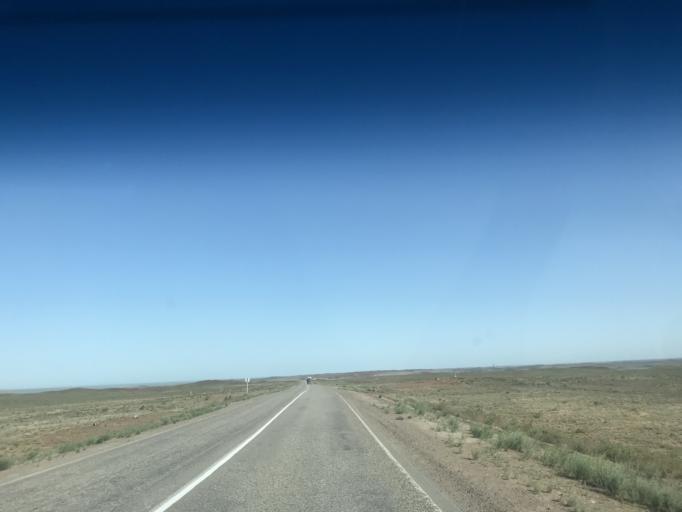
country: KZ
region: Zhambyl
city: Mynaral
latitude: 45.4698
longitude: 73.5592
